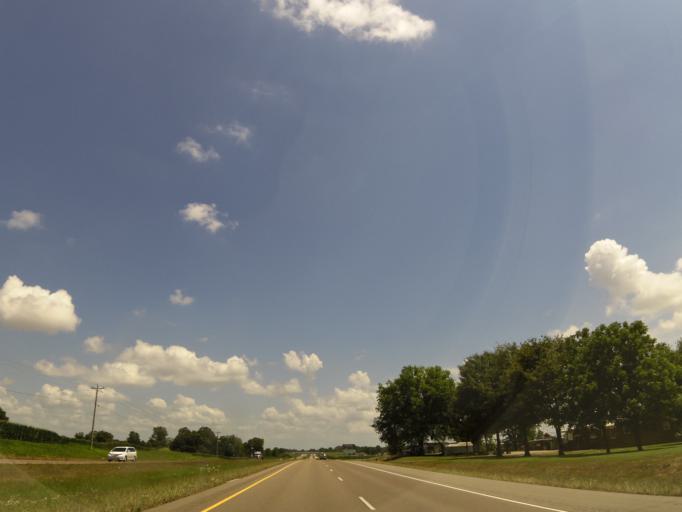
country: US
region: Tennessee
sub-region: Crockett County
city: Alamo
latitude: 35.8268
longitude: -89.1756
